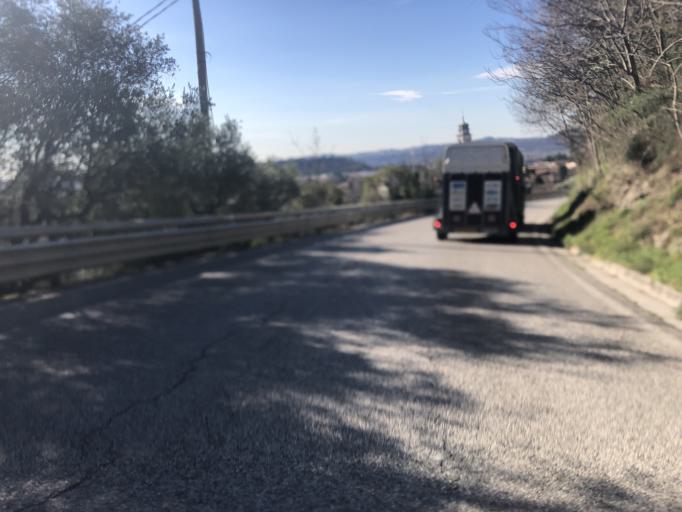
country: IT
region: Veneto
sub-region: Provincia di Verona
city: Sant'Ambrogio di Valpollicella
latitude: 45.5294
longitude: 10.8390
